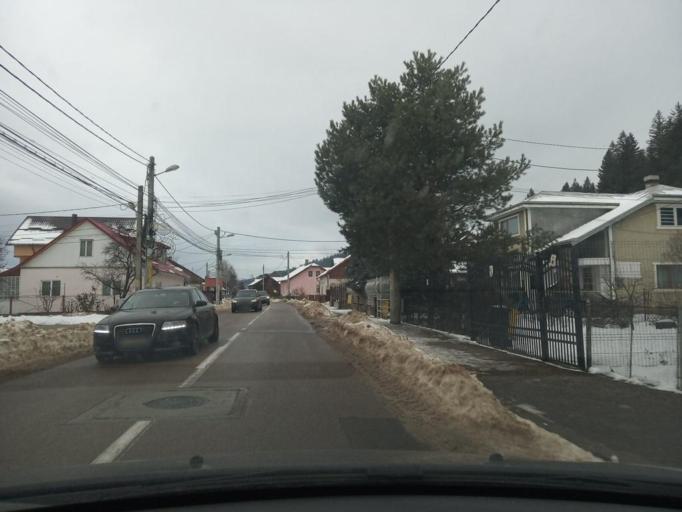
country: RO
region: Suceava
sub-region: Oras Gura Humorului
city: Gura Humorului
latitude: 47.5623
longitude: 25.8859
